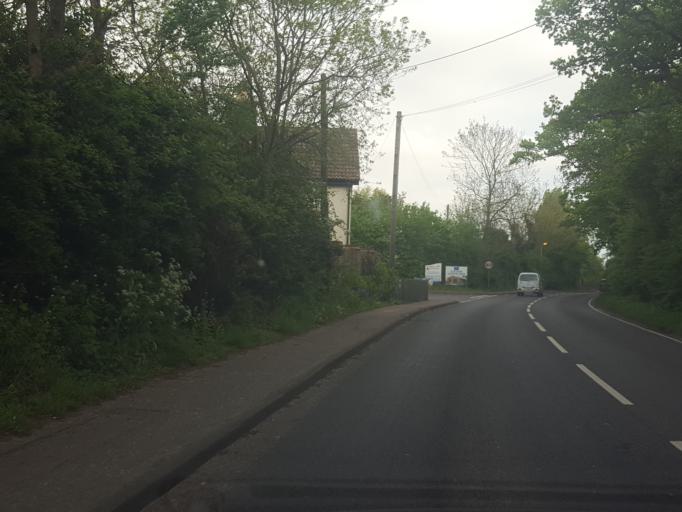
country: GB
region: England
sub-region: Essex
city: Little Clacton
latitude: 51.8554
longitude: 1.1694
